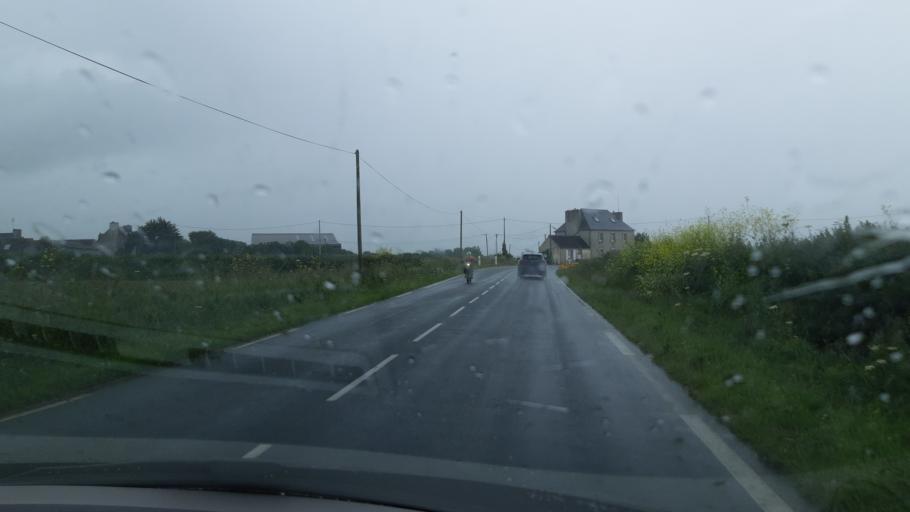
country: FR
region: Brittany
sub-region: Departement du Finistere
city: Saint-Pol-de-Leon
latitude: 48.6672
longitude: -4.0113
